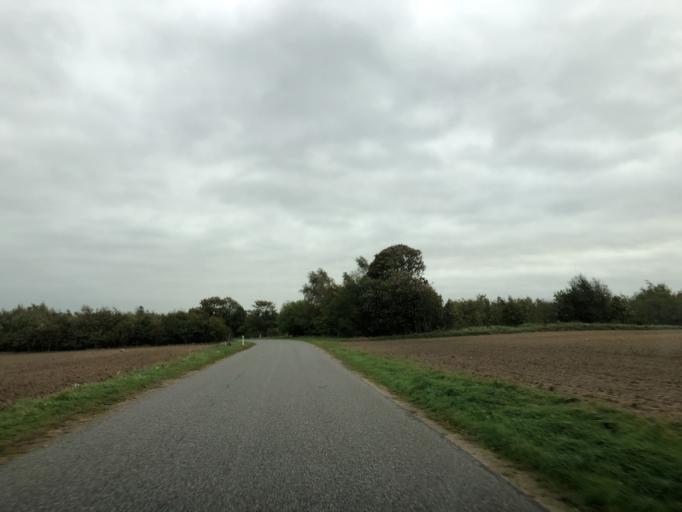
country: DK
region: Central Jutland
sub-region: Viborg Kommune
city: Viborg
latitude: 56.4184
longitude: 9.3144
